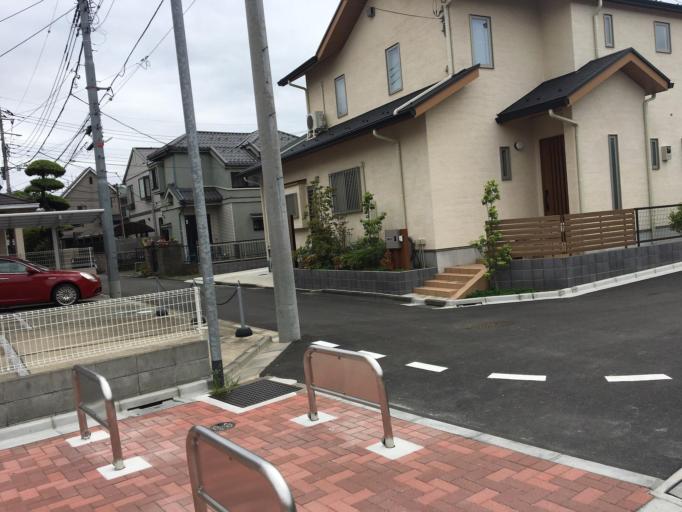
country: JP
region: Tokyo
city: Mitaka-shi
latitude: 35.6614
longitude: 139.5762
